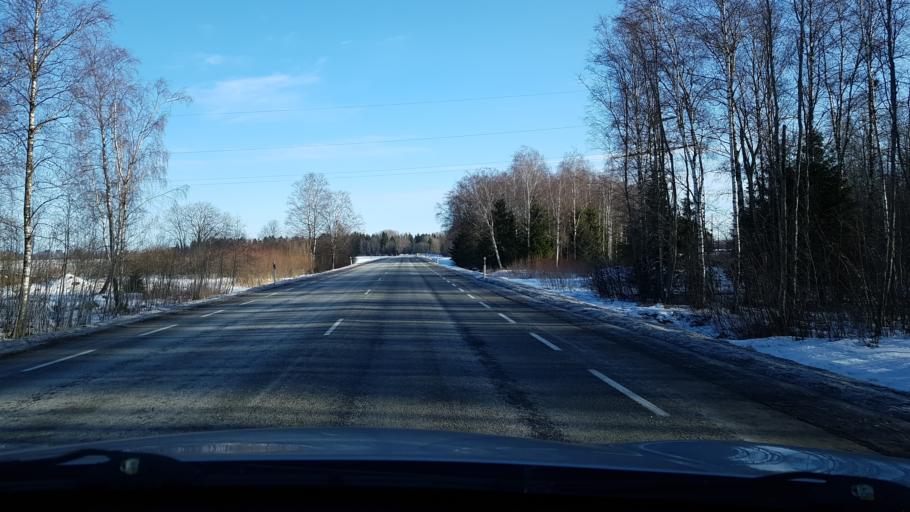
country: EE
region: Viljandimaa
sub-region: Vohma linn
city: Vohma
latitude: 58.6637
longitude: 25.6243
